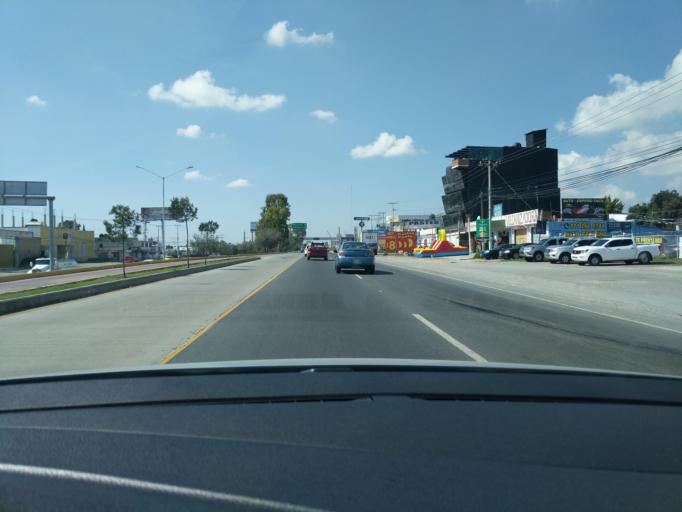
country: MX
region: Hidalgo
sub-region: Zempoala
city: Lindavista
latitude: 20.0349
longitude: -98.7995
